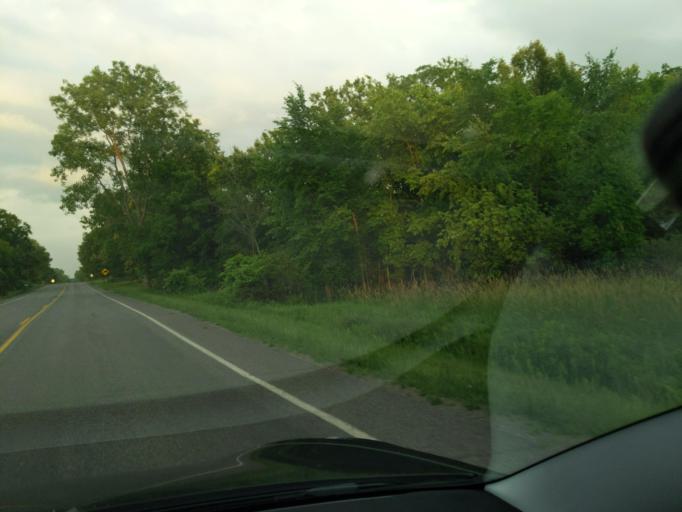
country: US
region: Michigan
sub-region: Ingham County
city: Mason
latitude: 42.5238
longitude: -84.3744
